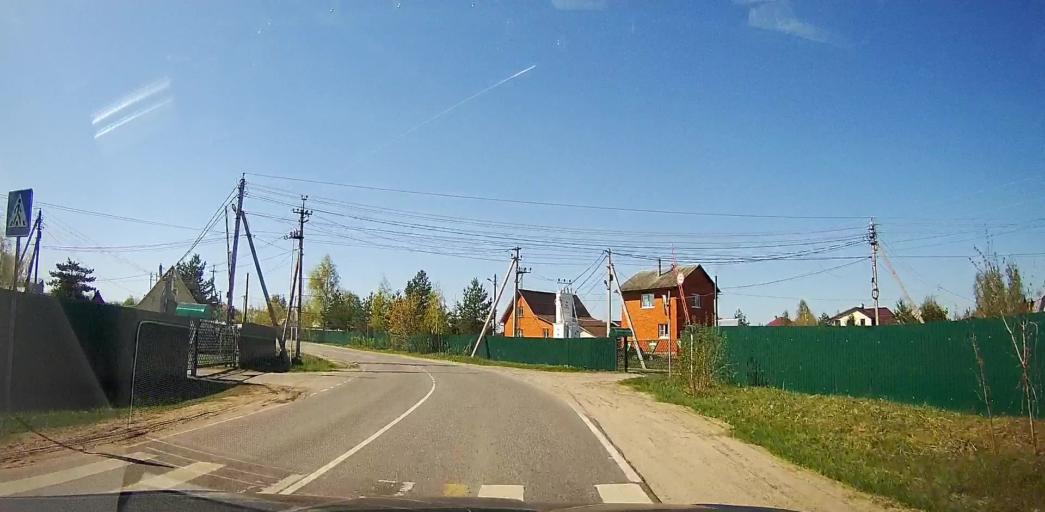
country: RU
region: Moskovskaya
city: Bronnitsy
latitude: 55.4725
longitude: 38.2612
